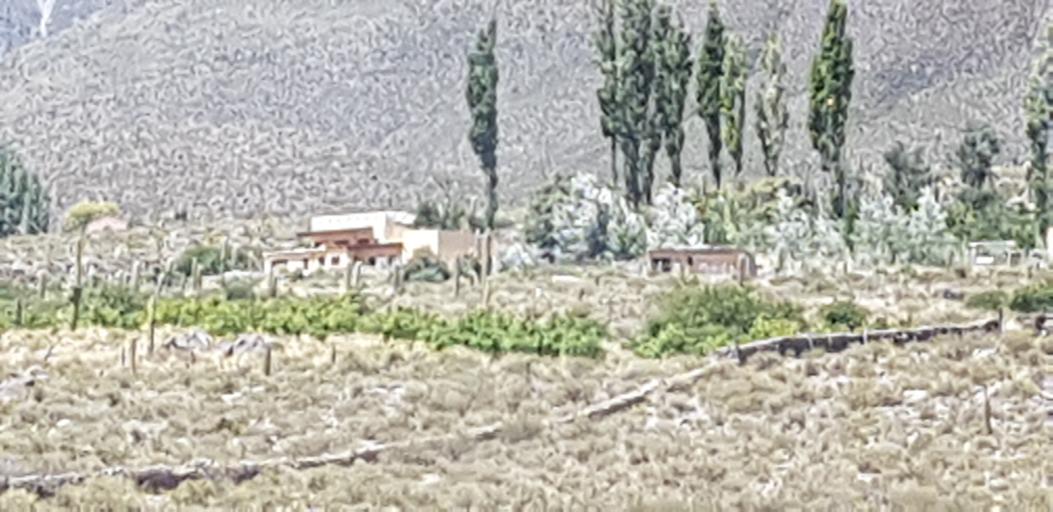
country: AR
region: Catamarca
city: Santa Maria
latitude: -26.6311
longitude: -65.8358
